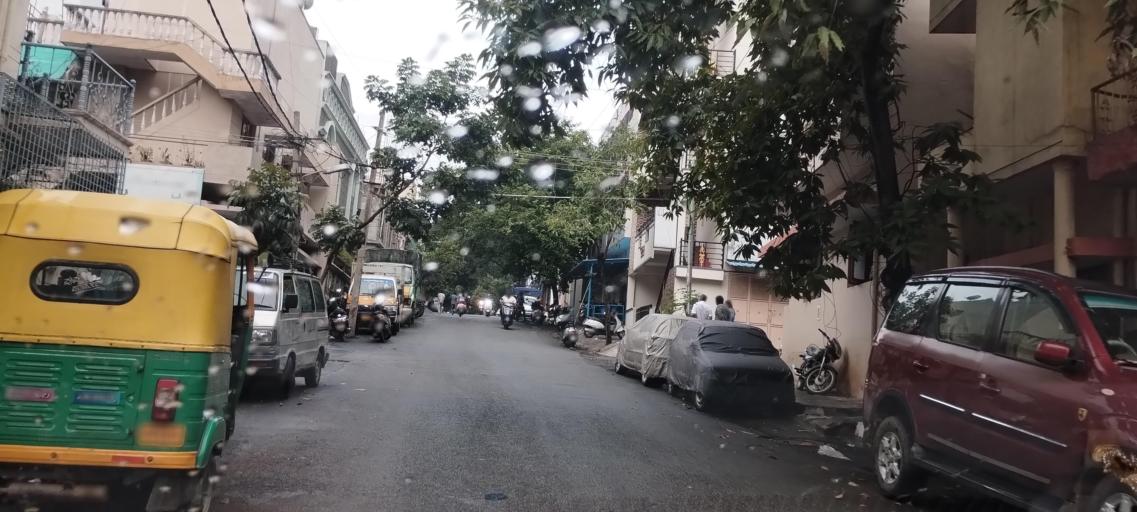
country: IN
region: Karnataka
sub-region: Bangalore Urban
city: Bangalore
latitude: 12.9399
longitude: 77.5524
